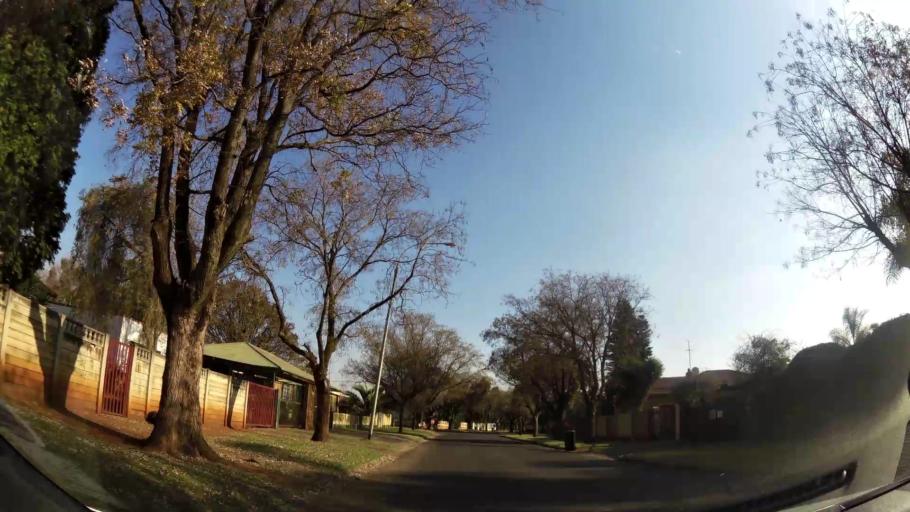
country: ZA
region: Gauteng
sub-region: Ekurhuleni Metropolitan Municipality
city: Brakpan
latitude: -26.2484
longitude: 28.3718
